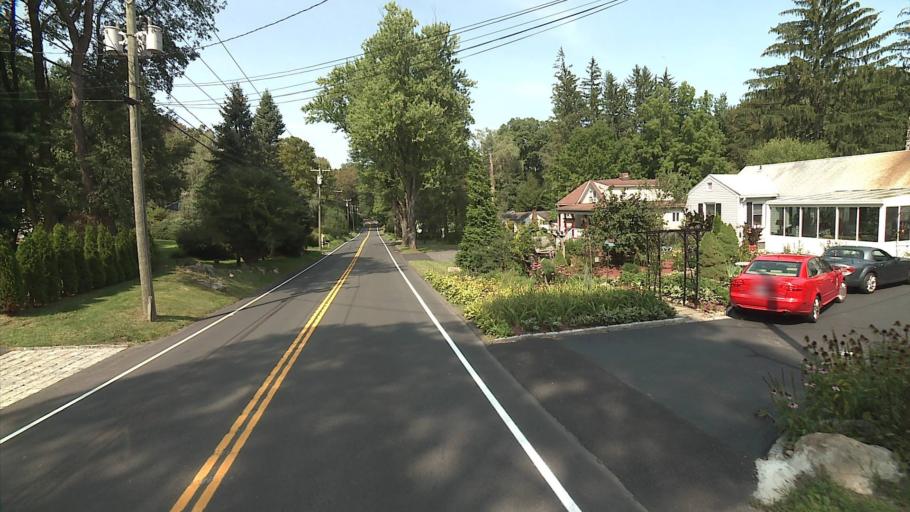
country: US
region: Connecticut
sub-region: Fairfield County
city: Bethel
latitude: 41.3695
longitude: -73.3906
